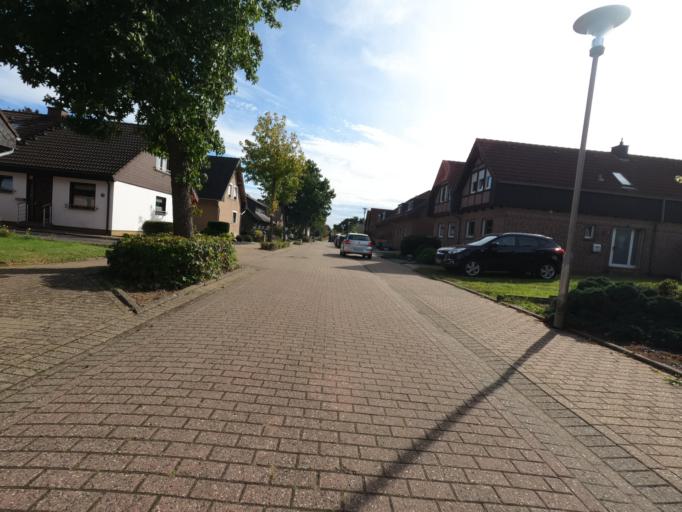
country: DE
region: North Rhine-Westphalia
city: Baesweiler
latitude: 50.9284
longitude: 6.1944
